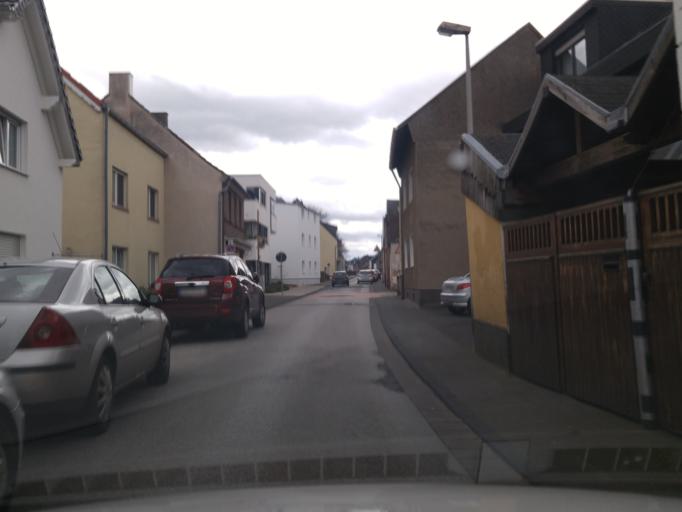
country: DE
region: North Rhine-Westphalia
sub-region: Regierungsbezirk Dusseldorf
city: Dormagen
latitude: 51.1395
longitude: 6.8182
